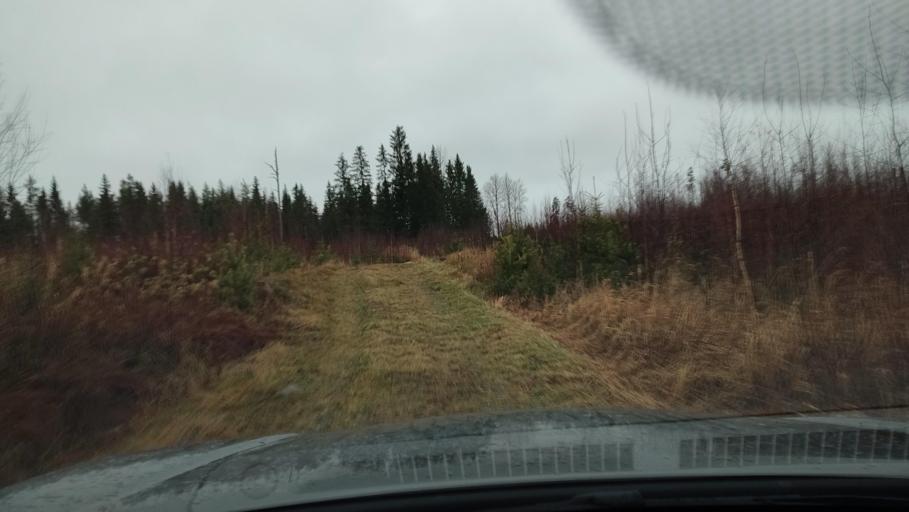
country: FI
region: Southern Ostrobothnia
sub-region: Suupohja
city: Karijoki
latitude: 62.2231
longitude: 21.5528
